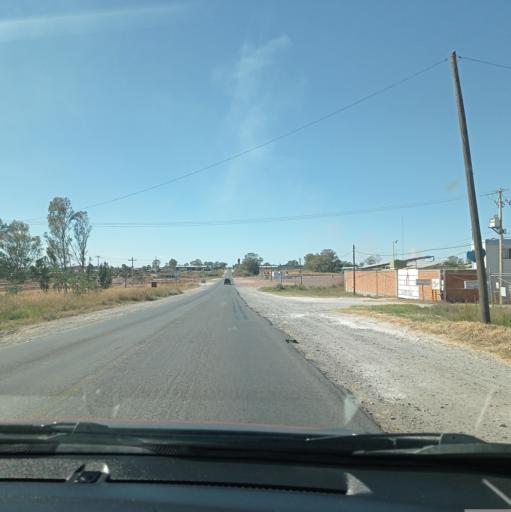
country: MX
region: Jalisco
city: San Julian
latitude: 21.0075
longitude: -102.1482
